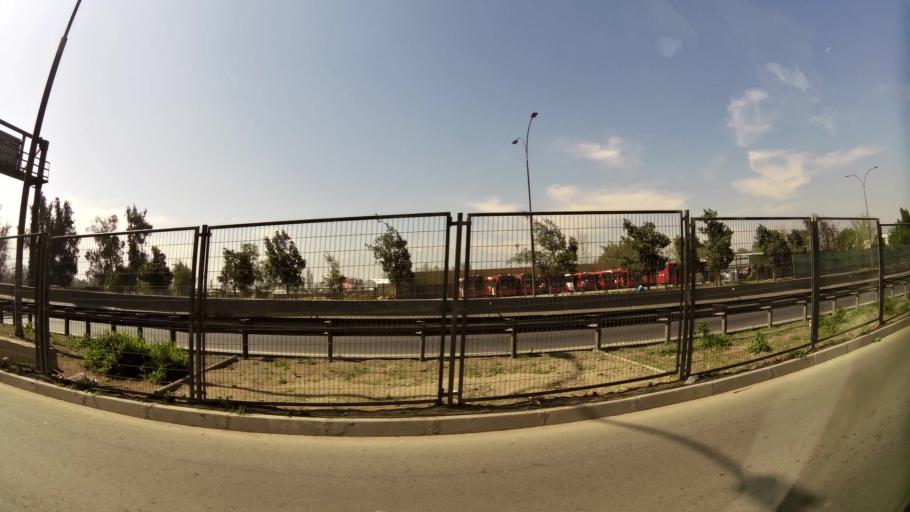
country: CL
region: Santiago Metropolitan
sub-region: Provincia de Santiago
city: Lo Prado
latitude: -33.3850
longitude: -70.6972
